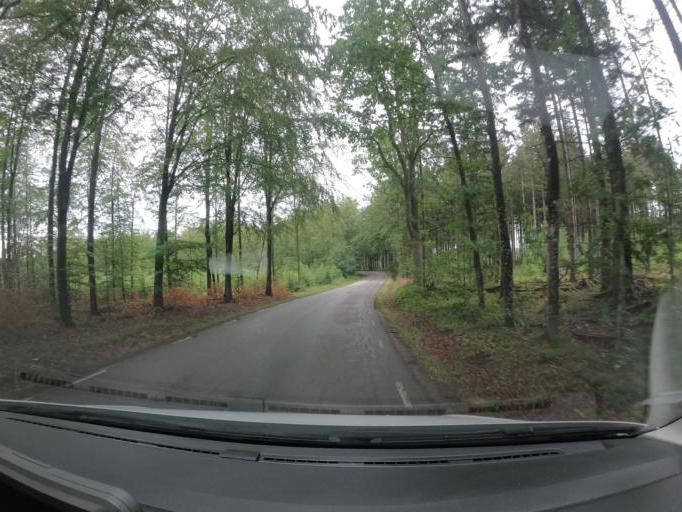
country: SE
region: Skane
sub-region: Angelholms Kommun
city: Munka-Ljungby
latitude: 56.2983
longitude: 13.1136
